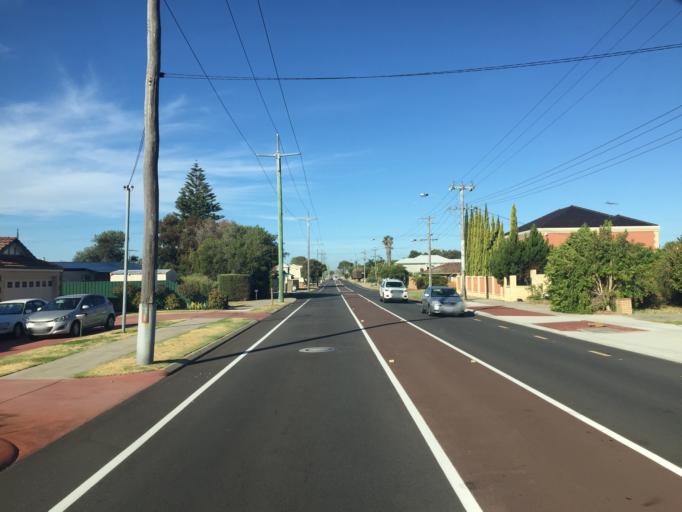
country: AU
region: Western Australia
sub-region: Belmont
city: Rivervale
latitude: -31.9645
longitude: 115.9242
